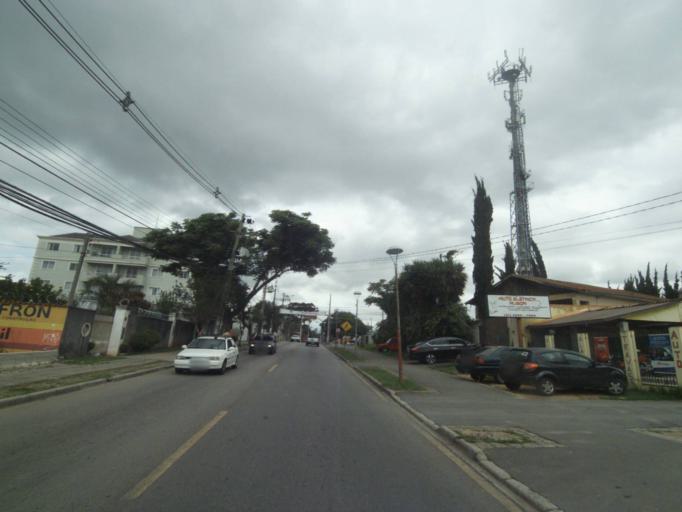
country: BR
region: Parana
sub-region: Curitiba
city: Curitiba
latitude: -25.3855
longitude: -49.2813
